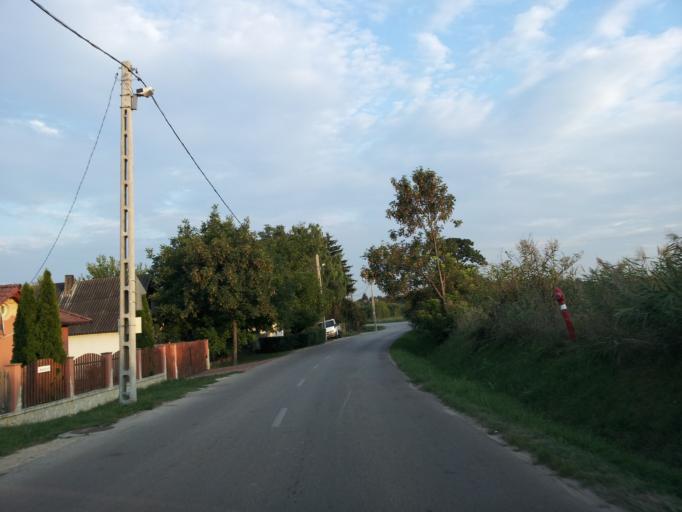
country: HU
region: Somogy
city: Siofok
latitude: 46.8916
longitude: 18.0529
